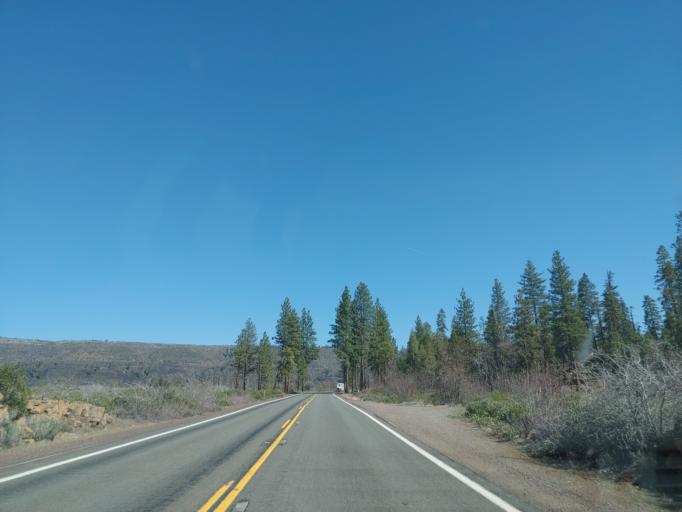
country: US
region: California
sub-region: Shasta County
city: Burney
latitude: 40.7300
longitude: -121.4342
